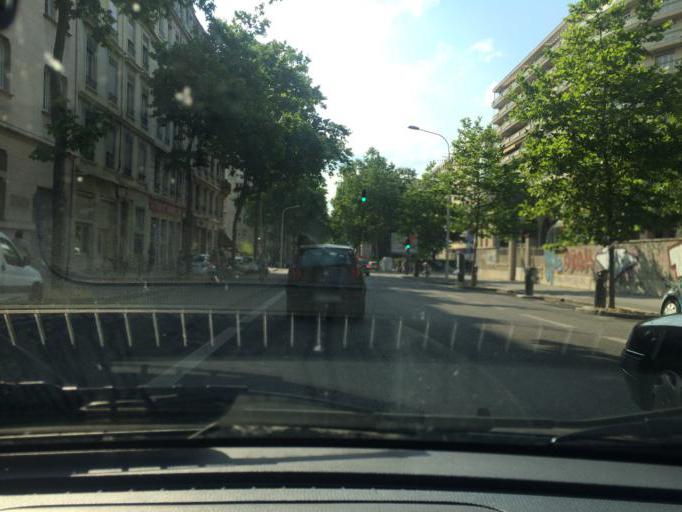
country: FR
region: Rhone-Alpes
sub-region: Departement du Rhone
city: Lyon
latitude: 45.7501
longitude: 4.8580
